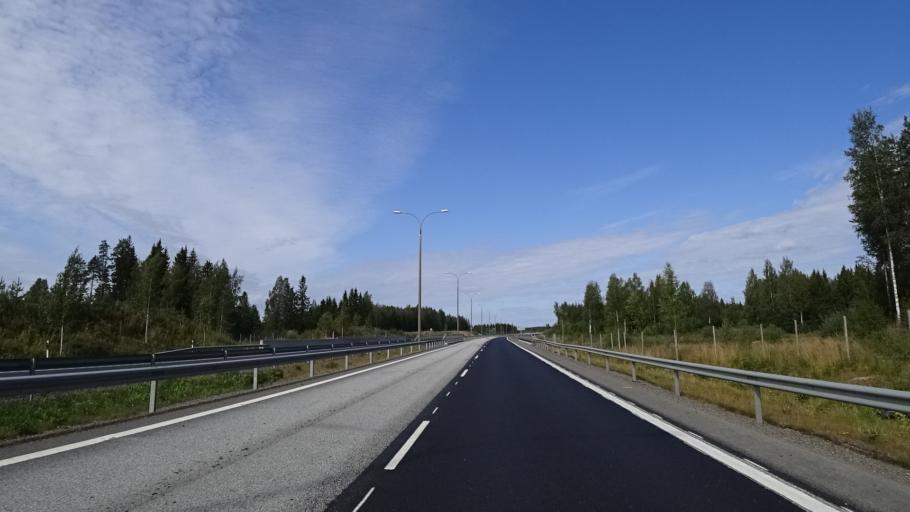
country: FI
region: North Karelia
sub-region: Joensuu
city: Joensuu
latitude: 62.5598
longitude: 29.8369
